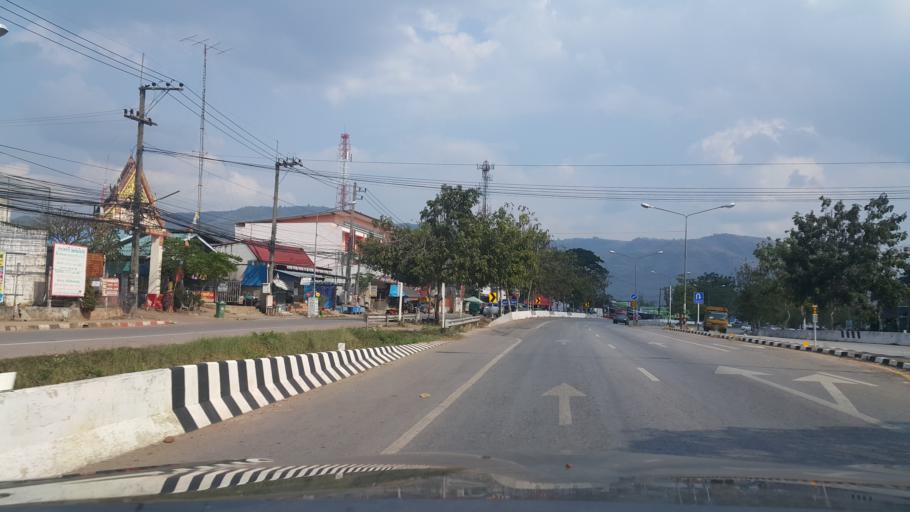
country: TH
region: Phitsanulok
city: Wang Thong
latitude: 16.8660
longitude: 100.6727
